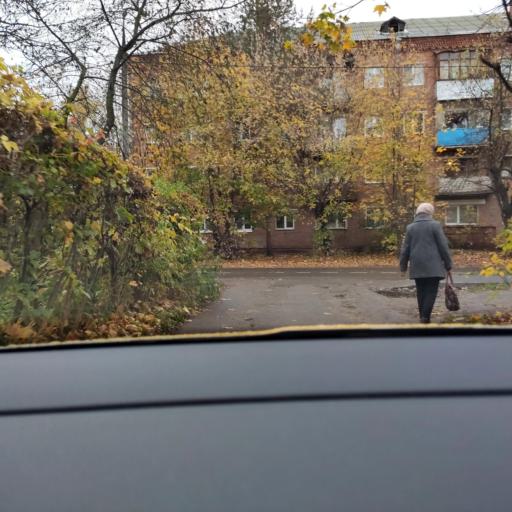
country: RU
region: Moskovskaya
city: Ivanteyevka
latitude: 55.9723
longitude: 37.8992
